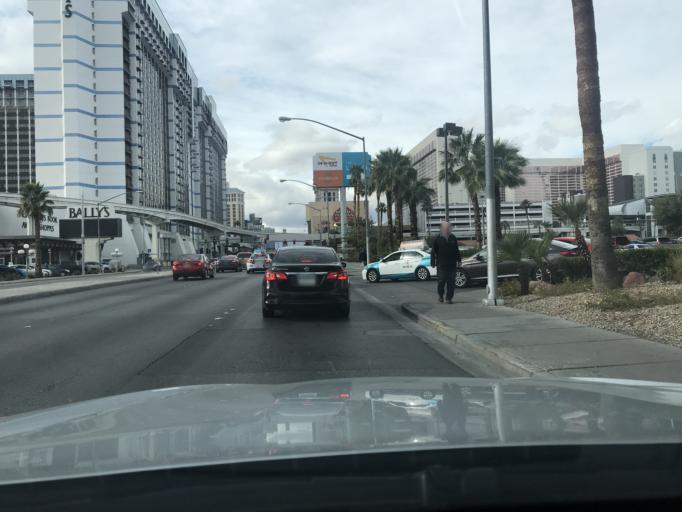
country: US
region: Nevada
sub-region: Clark County
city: Paradise
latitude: 36.1146
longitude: -115.1663
